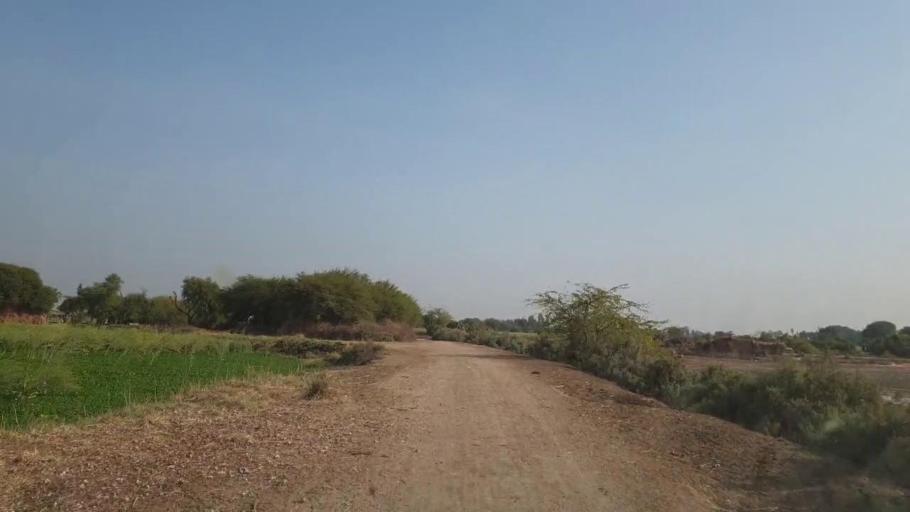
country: PK
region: Sindh
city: Pithoro
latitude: 25.6759
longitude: 69.2377
